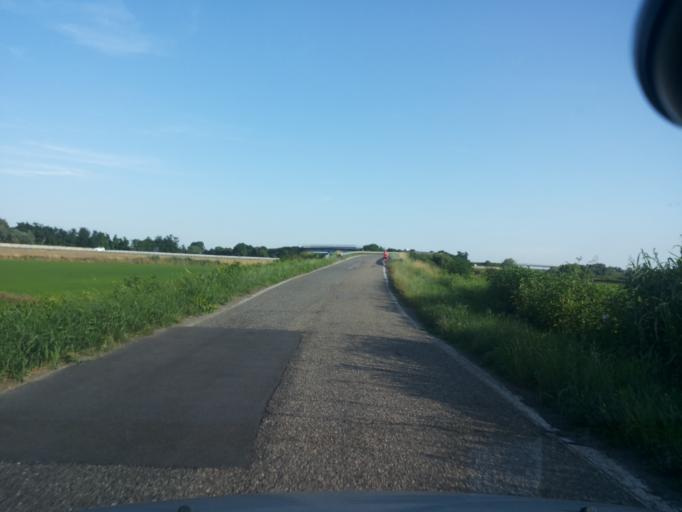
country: IT
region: Piedmont
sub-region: Provincia di Vercelli
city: Prarolo
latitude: 45.2724
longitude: 8.4679
